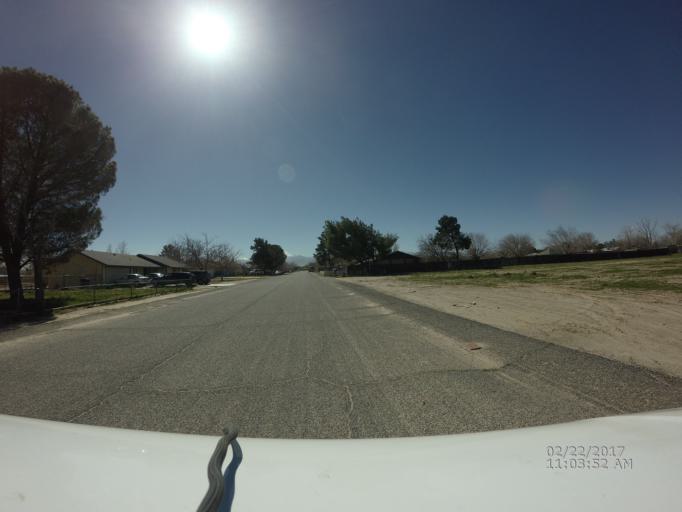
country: US
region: California
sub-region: Los Angeles County
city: Lake Los Angeles
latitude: 34.6278
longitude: -117.8128
